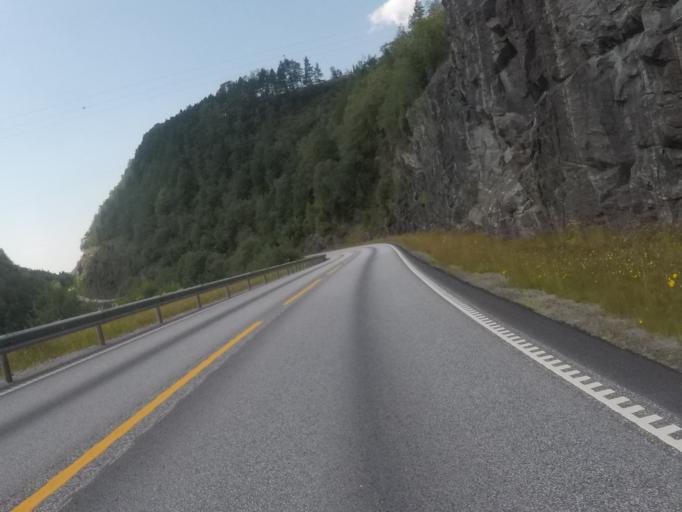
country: NO
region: Sogn og Fjordane
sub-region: Bremanger
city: Svelgen
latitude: 61.6118
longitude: 5.3183
